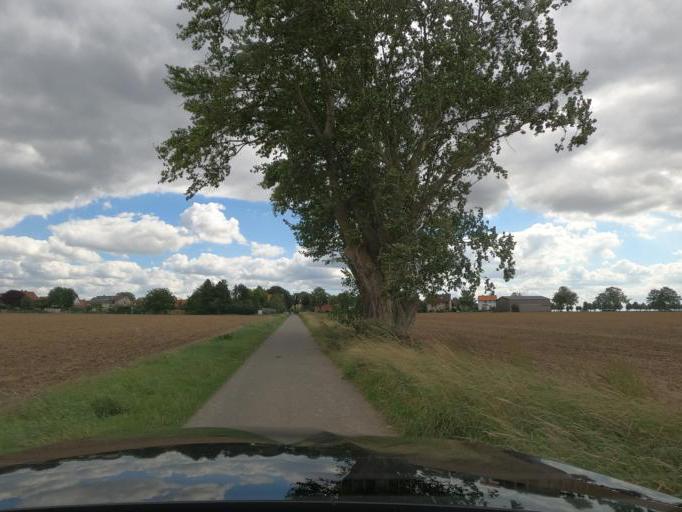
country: DE
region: Lower Saxony
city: Ilsede
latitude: 52.2531
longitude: 10.1571
